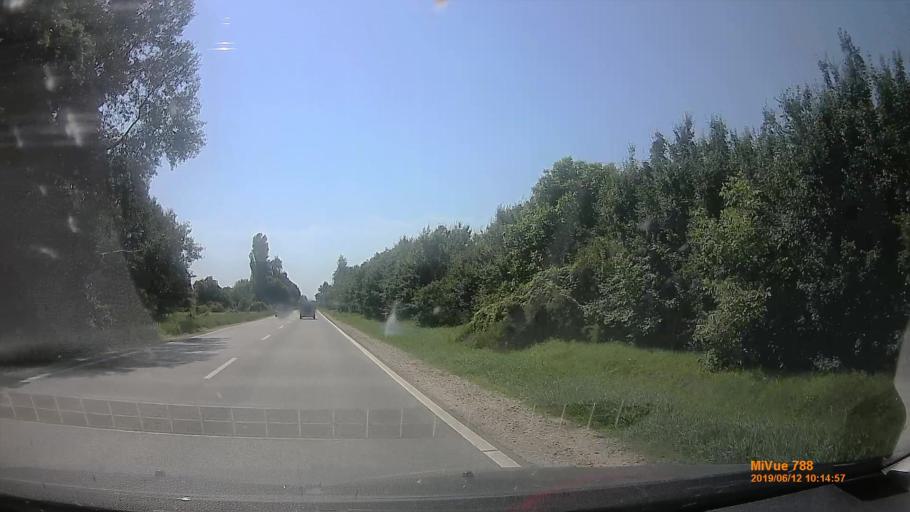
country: HU
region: Pest
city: Dabas
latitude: 47.2081
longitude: 19.2878
